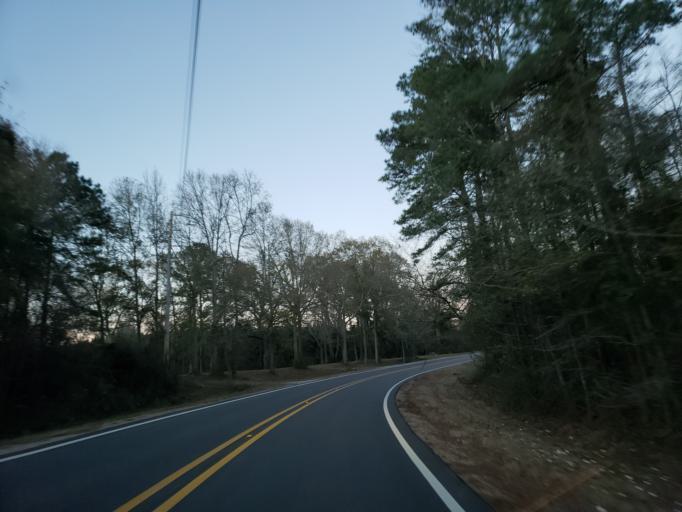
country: US
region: Mississippi
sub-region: Jones County
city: Ellisville
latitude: 31.5788
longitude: -89.2836
